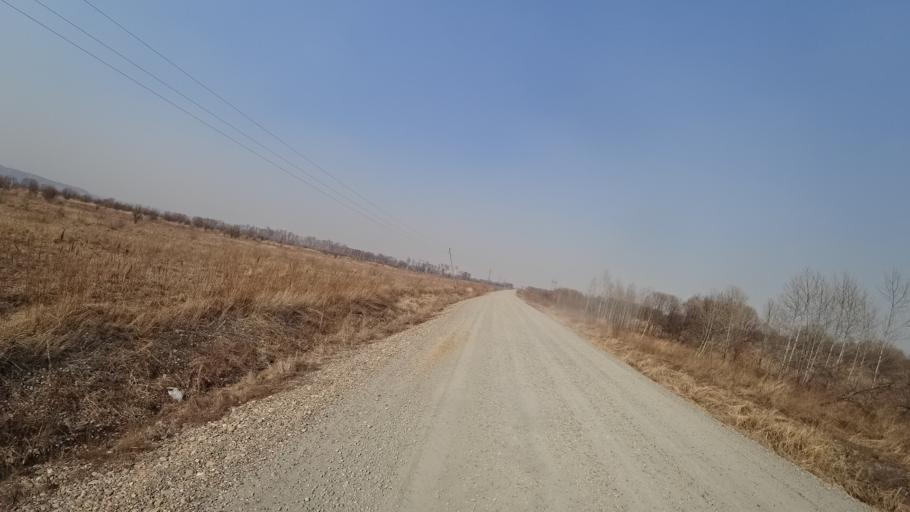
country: RU
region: Amur
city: Novobureyskiy
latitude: 49.8102
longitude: 129.9686
